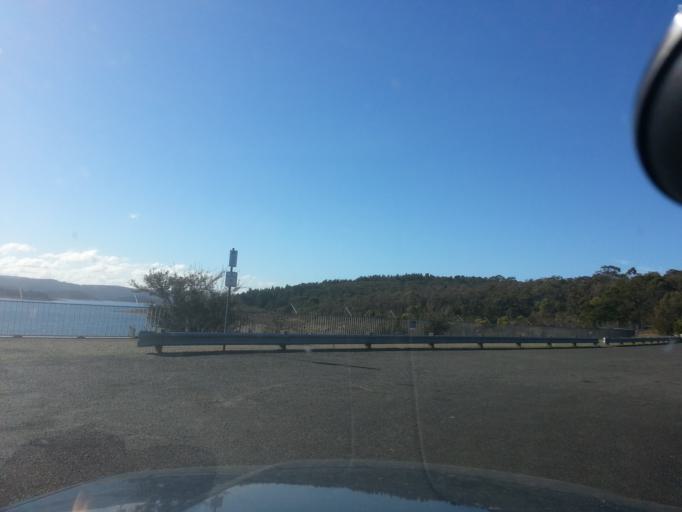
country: AU
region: Victoria
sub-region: Cardinia
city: Beaconsfield Upper
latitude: -37.9745
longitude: 145.3995
